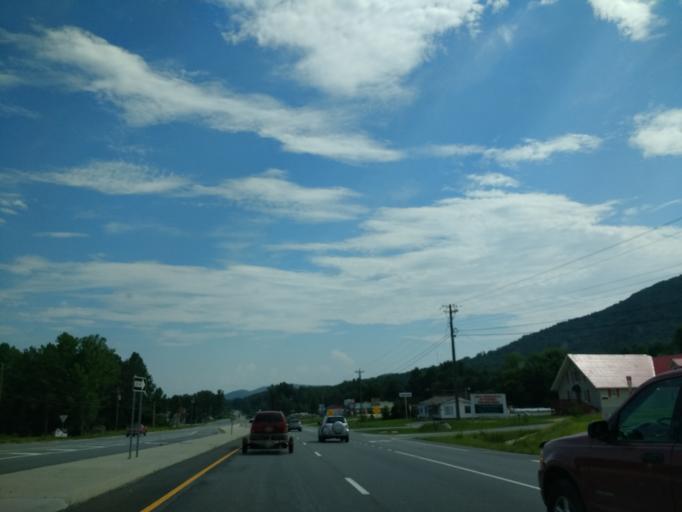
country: US
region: Georgia
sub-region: White County
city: Cleveland
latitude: 34.5759
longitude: -83.7628
